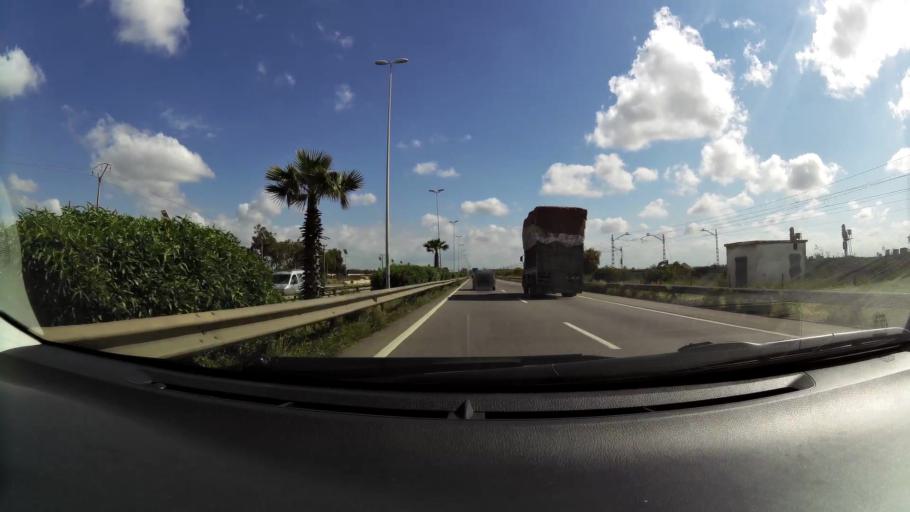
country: MA
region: Chaouia-Ouardigha
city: Nouaseur
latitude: 33.4174
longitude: -7.6268
